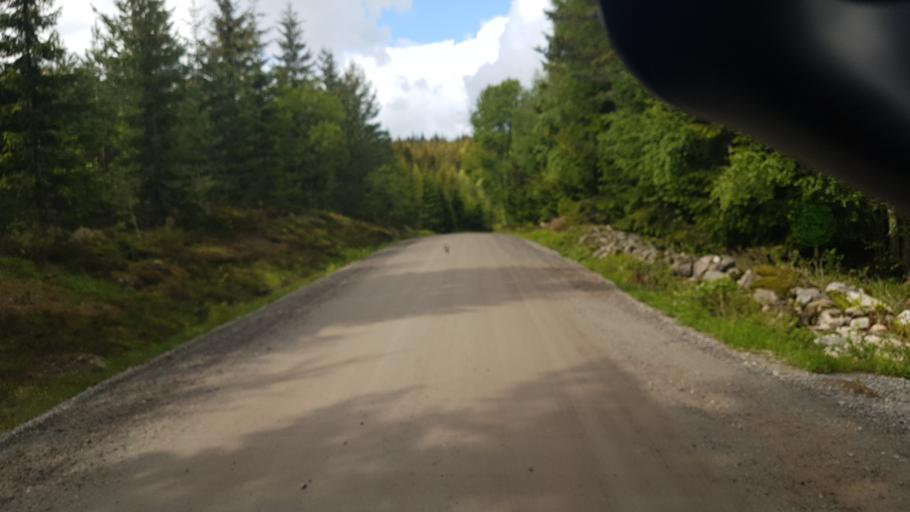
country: NO
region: Ostfold
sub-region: Romskog
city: Romskog
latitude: 59.7127
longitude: 12.0045
